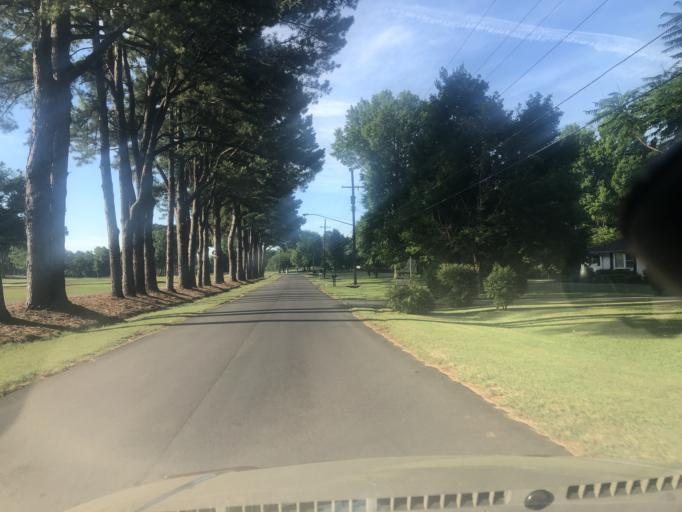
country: US
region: Tennessee
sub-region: Davidson County
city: Lakewood
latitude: 36.2496
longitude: -86.6514
